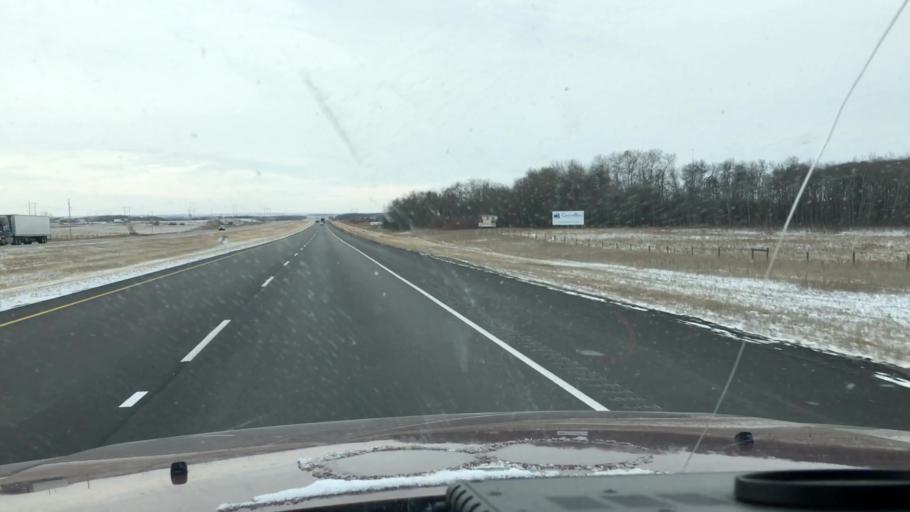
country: CA
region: Saskatchewan
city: Saskatoon
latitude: 51.9020
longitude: -106.5223
